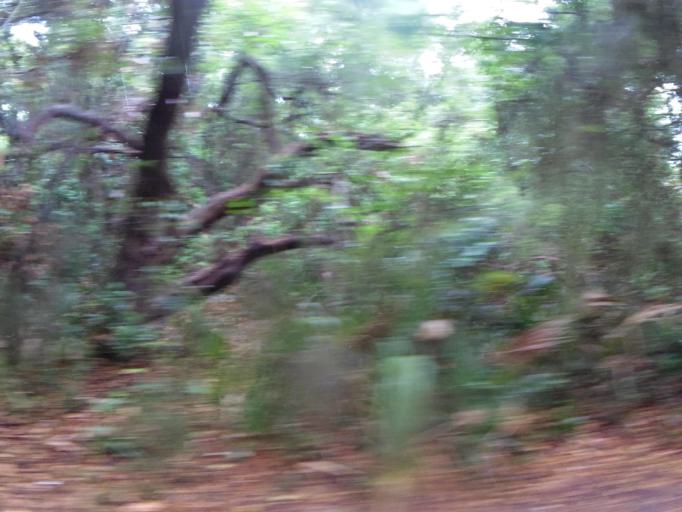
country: US
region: Florida
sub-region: Nassau County
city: Fernandina Beach
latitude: 30.6837
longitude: -81.4354
